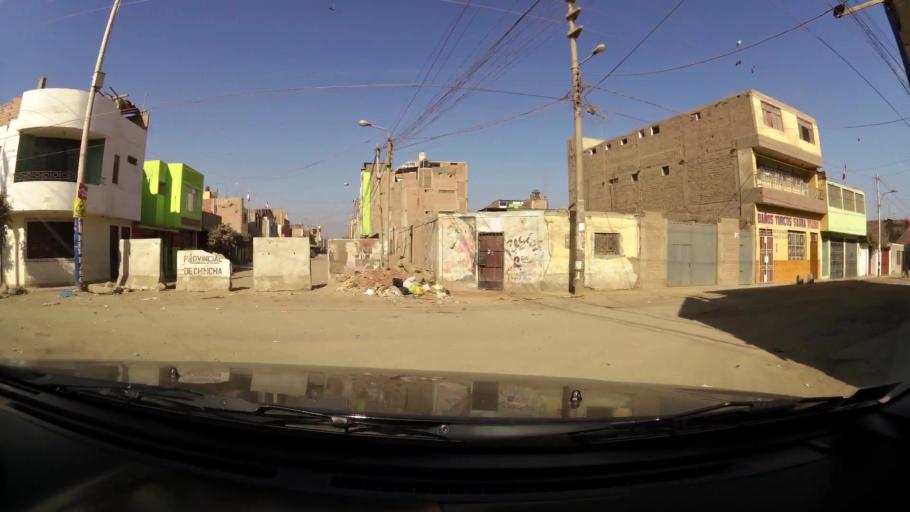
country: PE
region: Ica
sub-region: Provincia de Chincha
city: Chincha Alta
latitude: -13.4144
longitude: -76.1394
